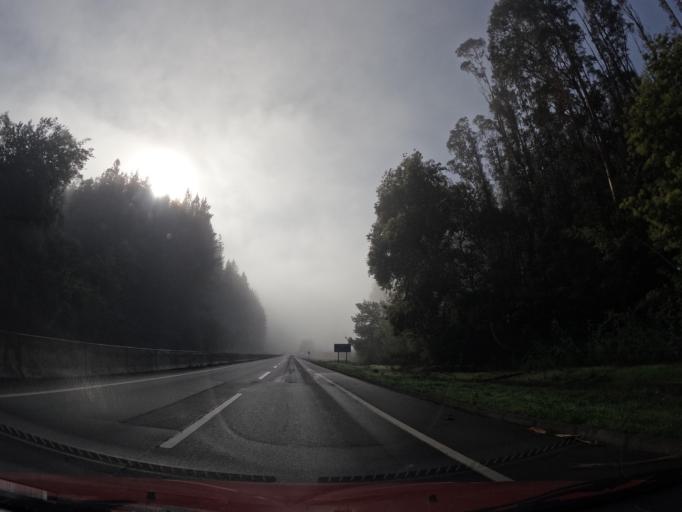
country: CL
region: Biobio
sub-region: Provincia de Concepcion
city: Penco
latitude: -36.7289
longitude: -72.8425
